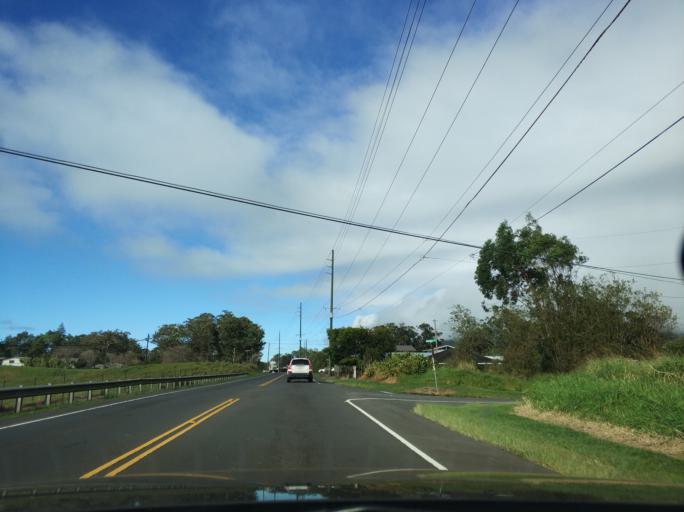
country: US
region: Hawaii
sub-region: Hawaii County
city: Waimea
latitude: 20.0410
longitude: -155.6067
